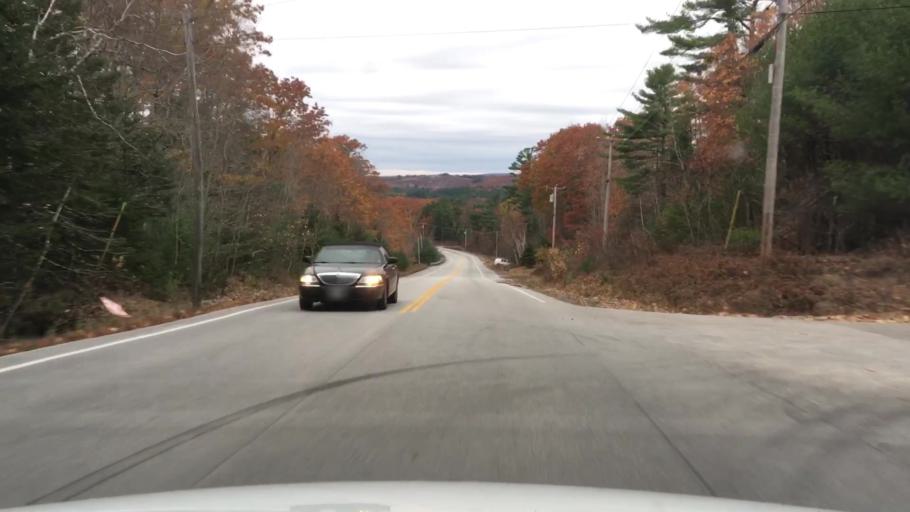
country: US
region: Maine
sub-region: Hancock County
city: Orland
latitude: 44.5551
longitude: -68.6955
